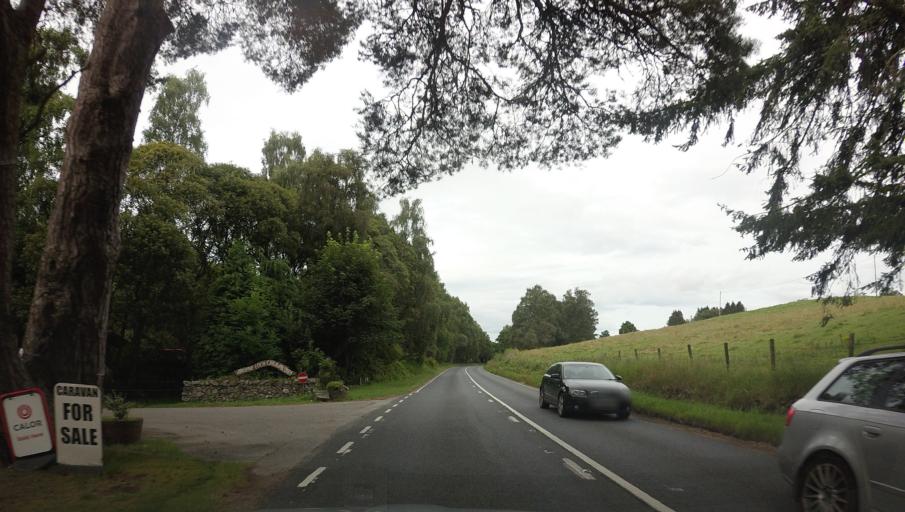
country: GB
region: Scotland
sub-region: Aberdeenshire
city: Aboyne
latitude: 57.0853
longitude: -2.7636
